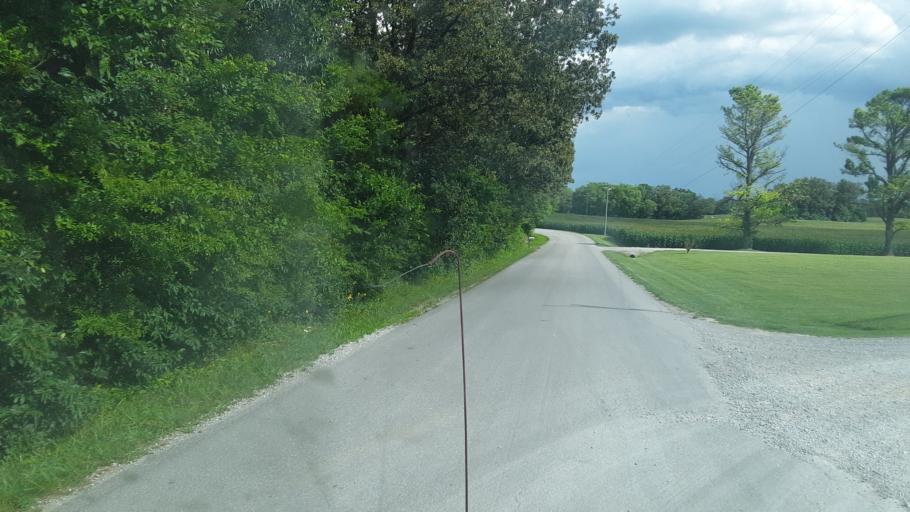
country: US
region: Kentucky
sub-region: Todd County
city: Elkton
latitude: 36.7496
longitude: -87.1707
